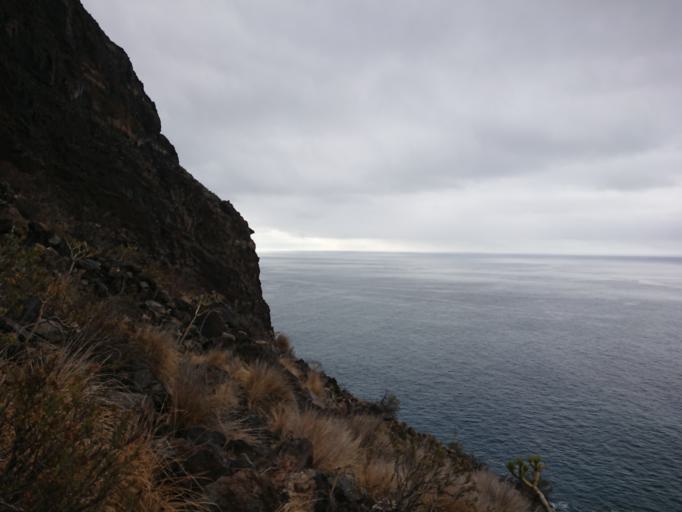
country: ES
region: Canary Islands
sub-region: Provincia de Santa Cruz de Tenerife
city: Tijarafe
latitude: 28.7191
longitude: -17.9786
